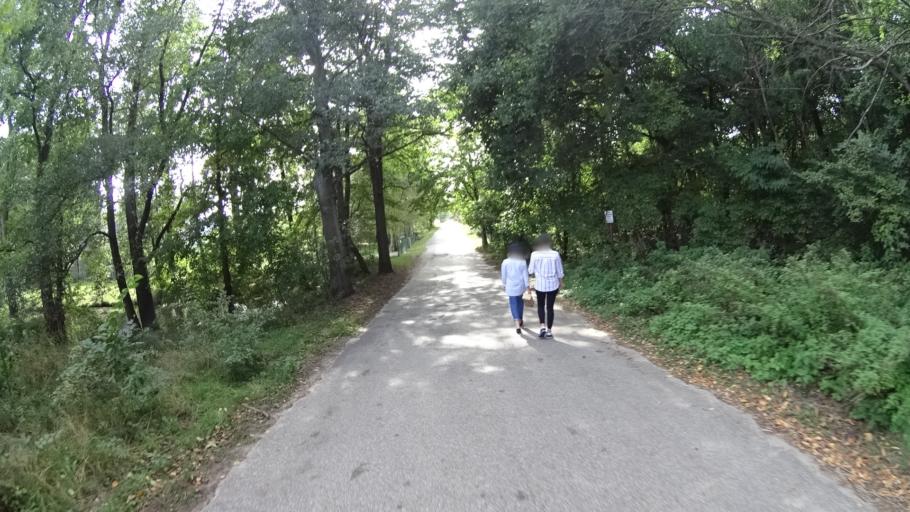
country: PL
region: Masovian Voivodeship
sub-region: Powiat legionowski
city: Serock
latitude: 52.4901
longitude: 21.0873
